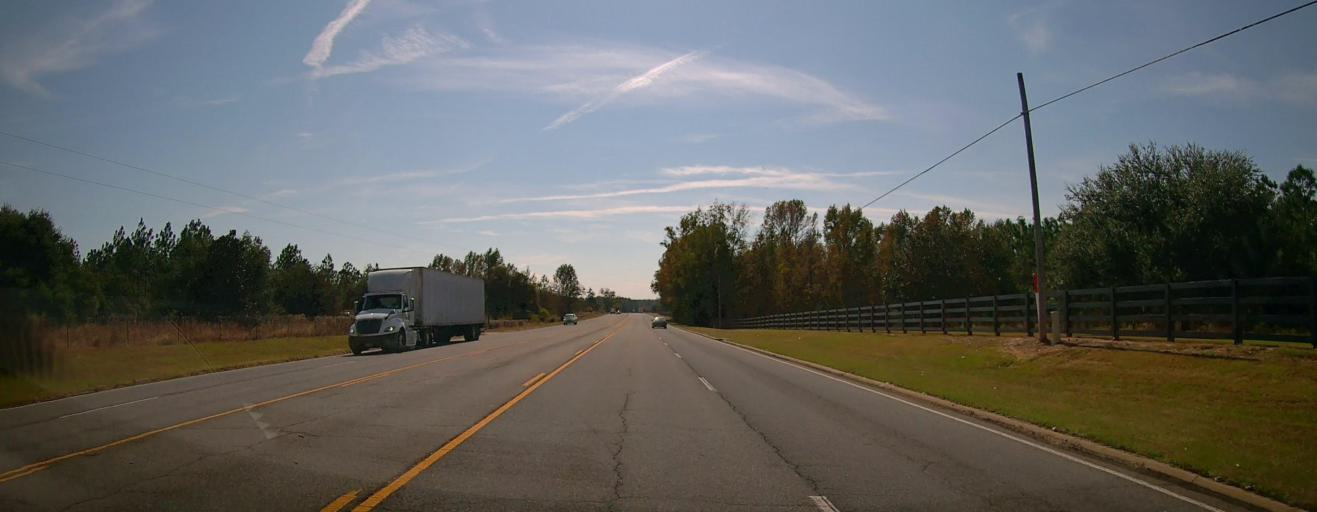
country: US
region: Georgia
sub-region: Lee County
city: Leesburg
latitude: 31.7704
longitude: -83.9713
